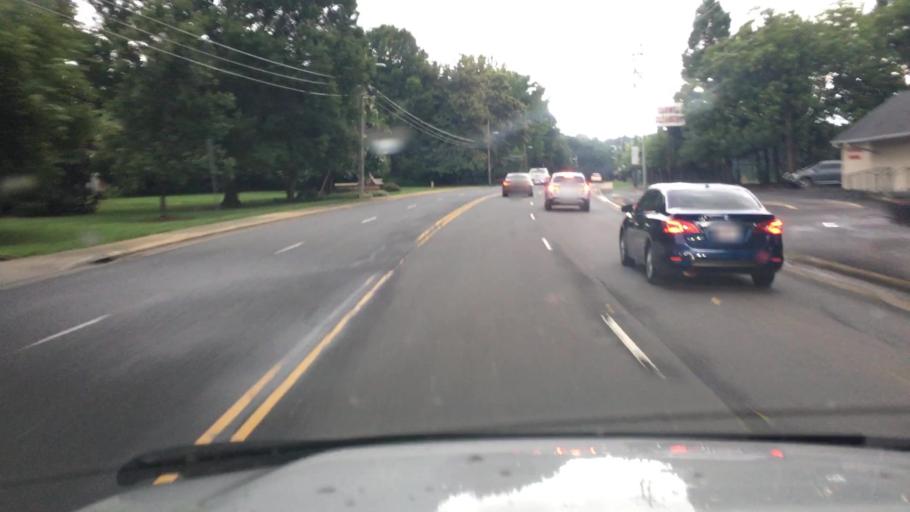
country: US
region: North Carolina
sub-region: Mecklenburg County
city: Matthews
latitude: 35.1442
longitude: -80.8014
